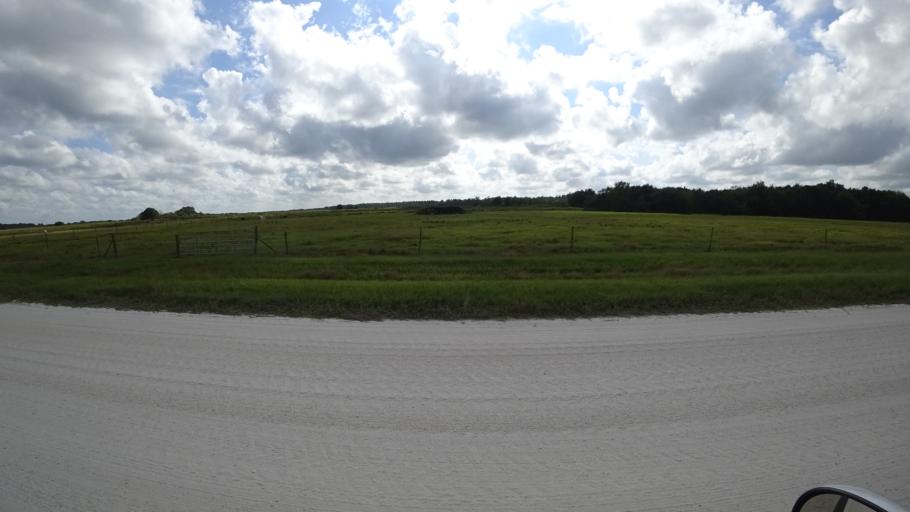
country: US
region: Florida
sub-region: Sarasota County
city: Lake Sarasota
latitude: 27.4263
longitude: -82.1847
